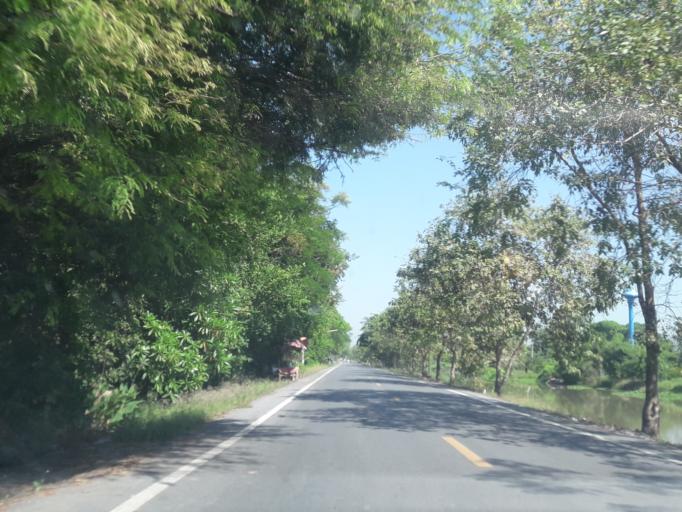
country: TH
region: Pathum Thani
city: Nong Suea
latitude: 14.1441
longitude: 100.8459
